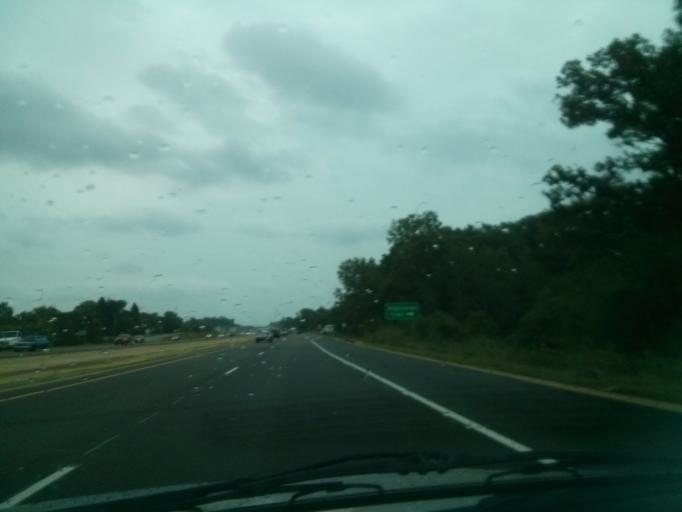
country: US
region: Minnesota
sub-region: Washington County
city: Mahtomedi
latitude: 45.0356
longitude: -92.9422
